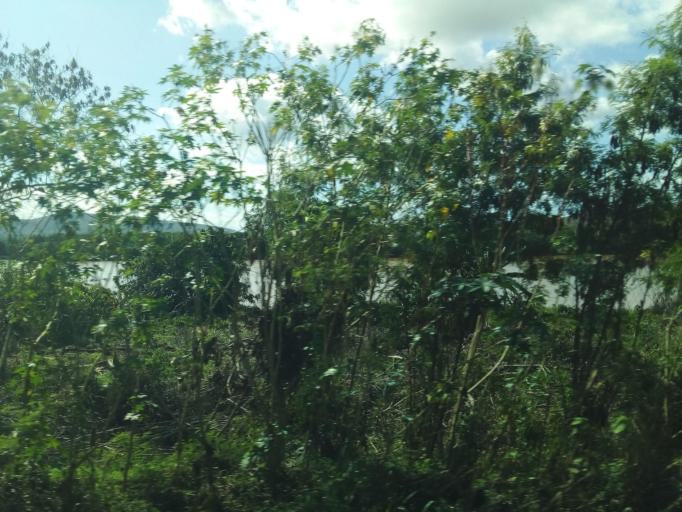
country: BR
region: Minas Gerais
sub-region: Governador Valadares
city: Governador Valadares
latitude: -18.8708
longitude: -41.7775
